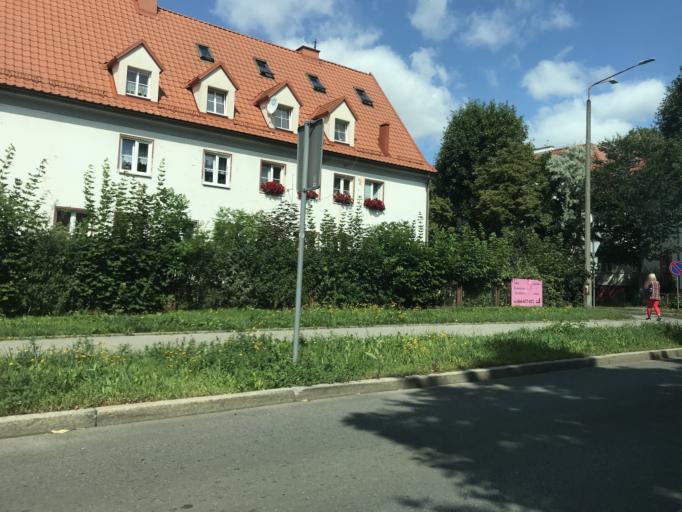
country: PL
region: Warmian-Masurian Voivodeship
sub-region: Powiat elblaski
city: Elblag
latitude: 54.1575
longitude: 19.4210
